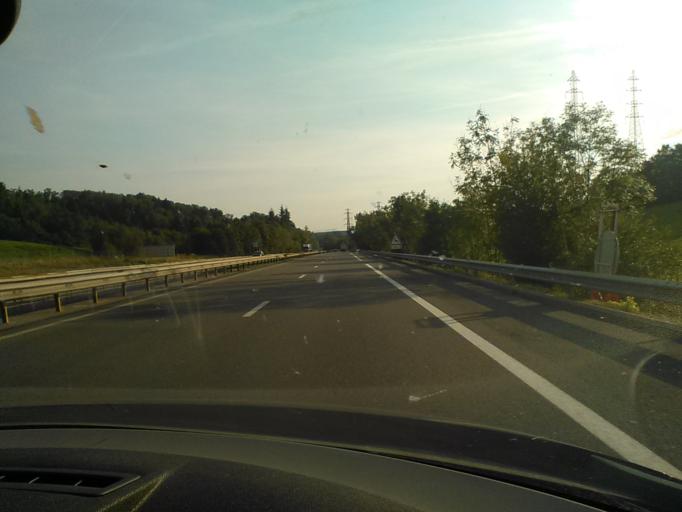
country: FR
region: Rhone-Alpes
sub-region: Departement de la Haute-Savoie
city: Seynod
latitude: 45.8725
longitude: 6.0663
